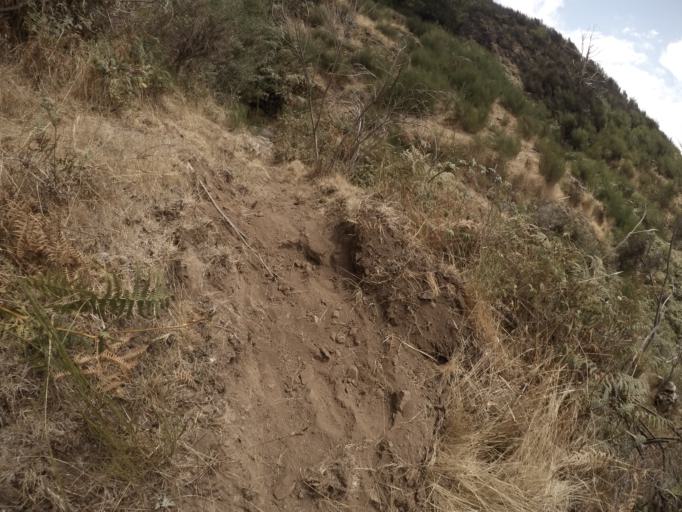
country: PT
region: Madeira
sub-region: Camara de Lobos
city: Curral das Freiras
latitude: 32.7105
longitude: -17.0047
